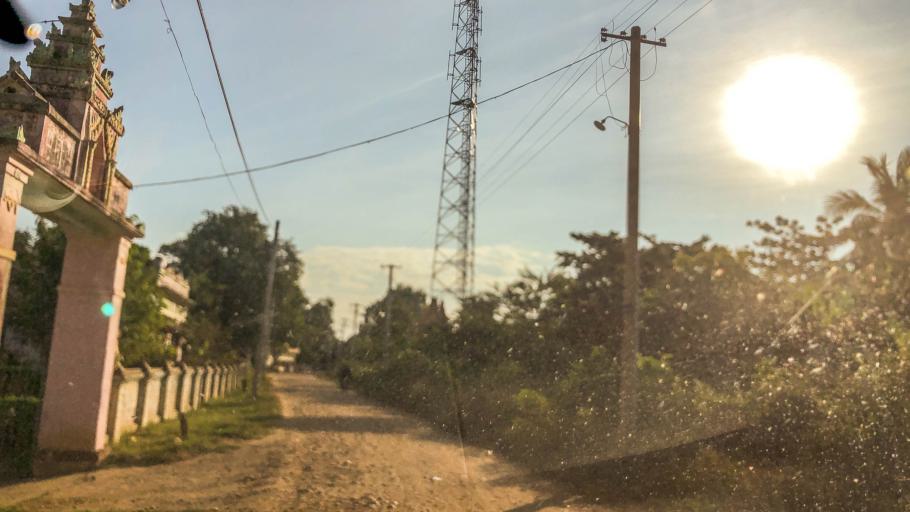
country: MM
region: Magway
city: Magway
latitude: 19.9754
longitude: 95.0352
